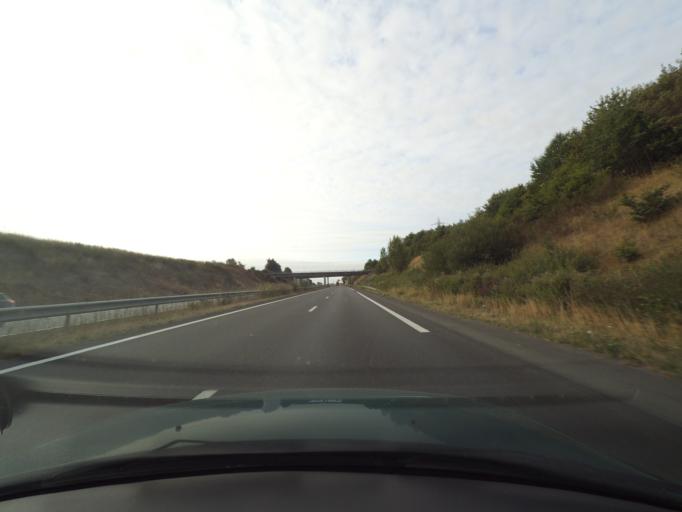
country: FR
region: Pays de la Loire
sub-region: Departement de Maine-et-Loire
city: La Seguiniere
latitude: 47.0511
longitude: -0.9185
